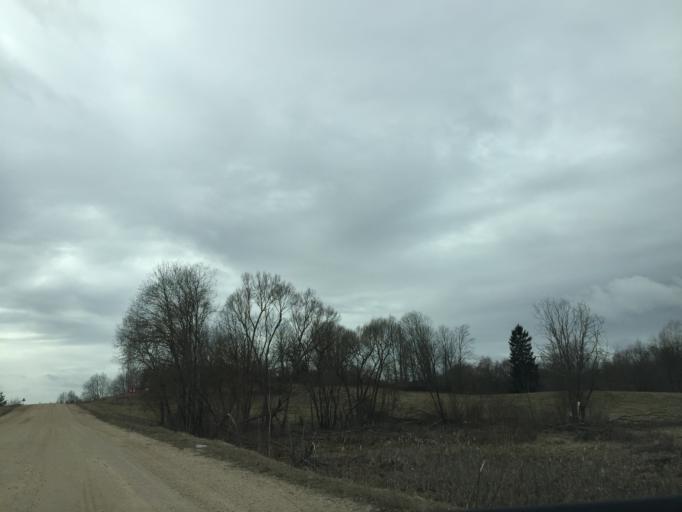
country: LV
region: Kraslavas Rajons
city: Kraslava
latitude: 55.9765
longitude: 27.0852
